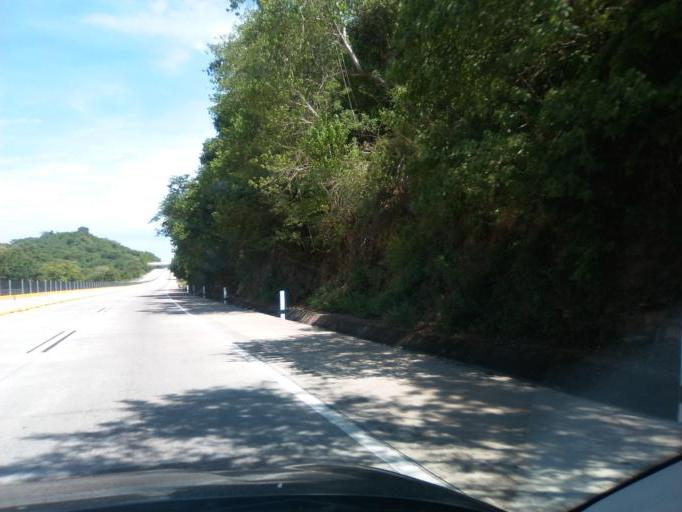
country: MX
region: Guerrero
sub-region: Acapulco de Juarez
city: Kilometro 30
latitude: 16.9775
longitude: -99.7194
